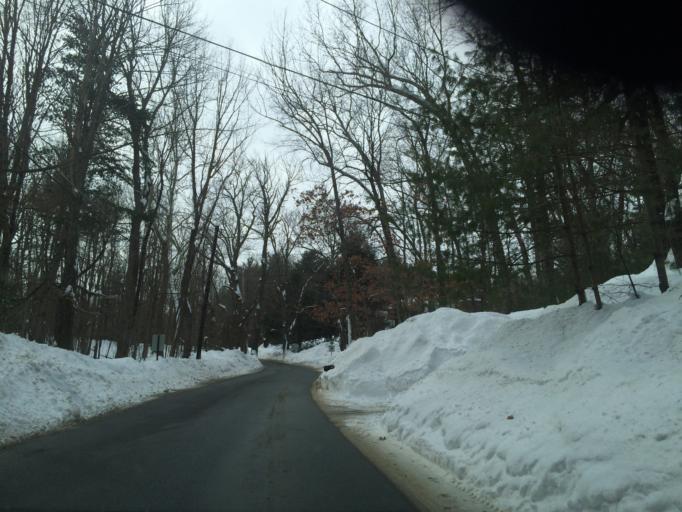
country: US
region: Massachusetts
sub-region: Middlesex County
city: Weston
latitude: 42.3934
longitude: -71.3212
